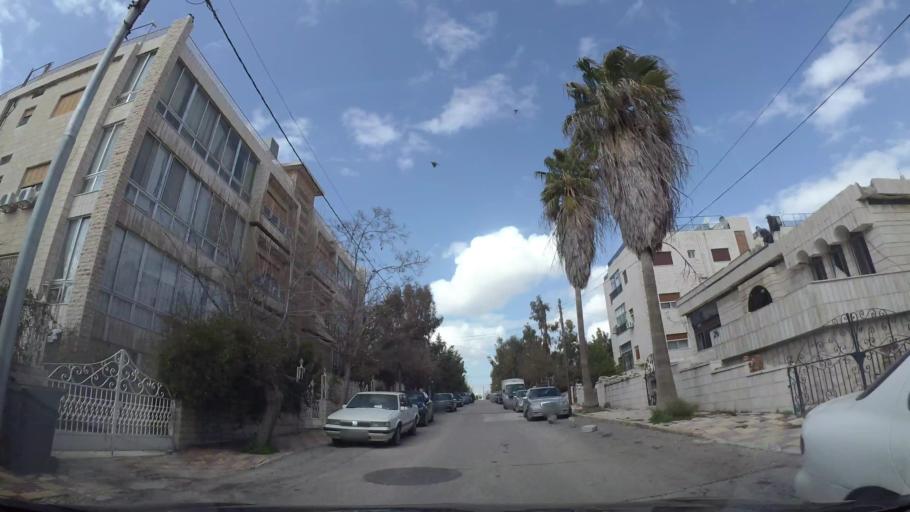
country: JO
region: Amman
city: Amman
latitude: 31.9709
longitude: 35.8946
